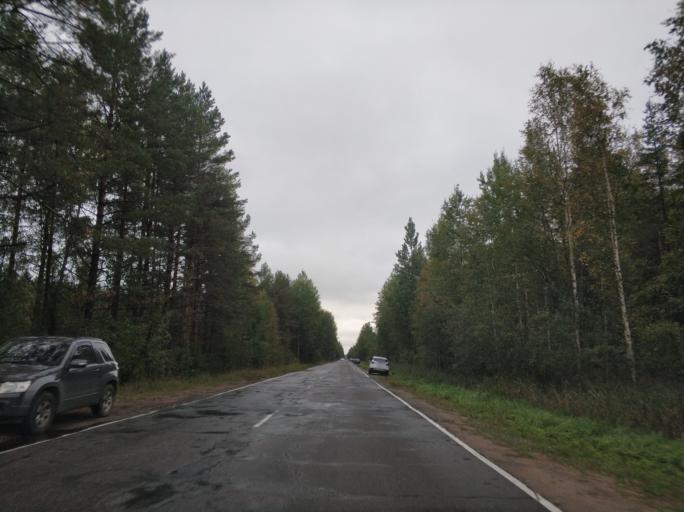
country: RU
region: Leningrad
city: Borisova Griva
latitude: 60.1672
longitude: 30.9207
